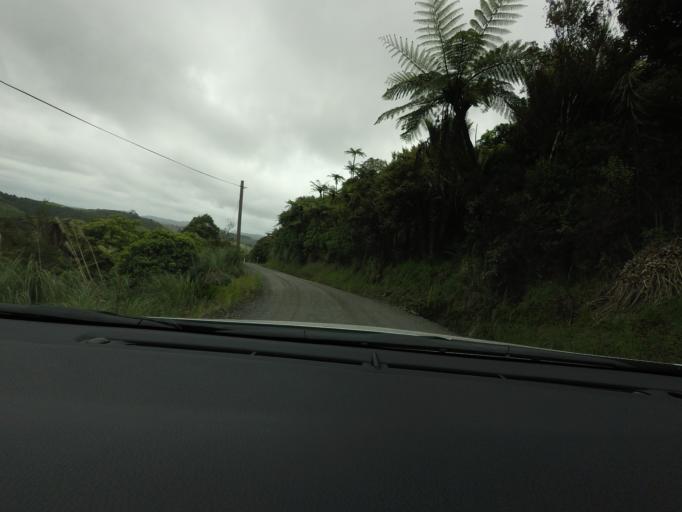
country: NZ
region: Auckland
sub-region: Auckland
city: Warkworth
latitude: -36.4817
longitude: 174.6002
